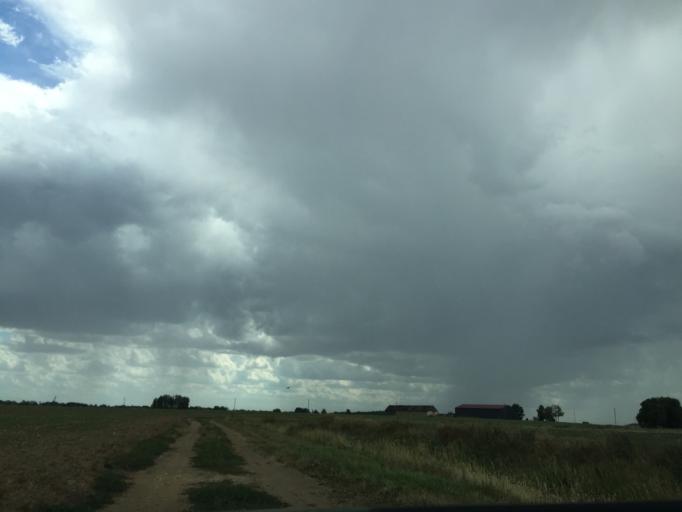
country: LT
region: Siauliu apskritis
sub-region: Joniskis
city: Joniskis
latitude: 56.2896
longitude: 23.7263
